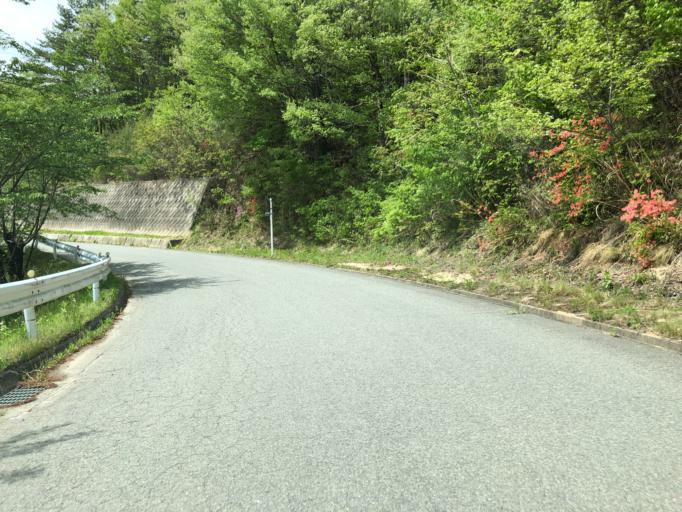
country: JP
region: Fukushima
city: Yanagawamachi-saiwaicho
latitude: 37.7190
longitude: 140.7148
